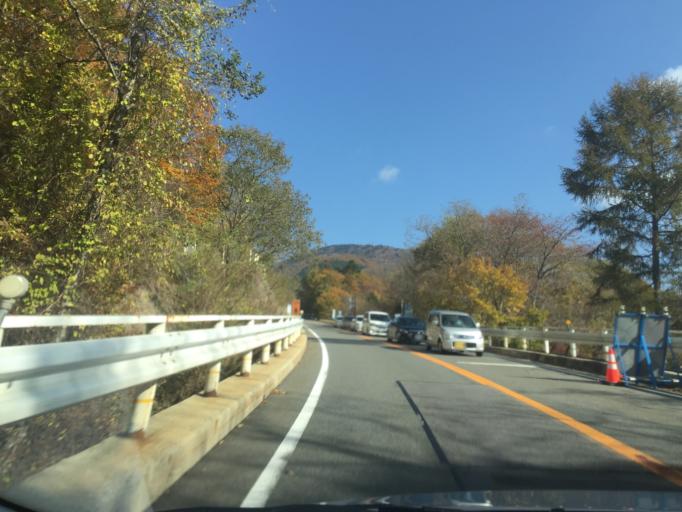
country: JP
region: Gifu
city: Nakatsugawa
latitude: 35.3429
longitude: 137.6540
